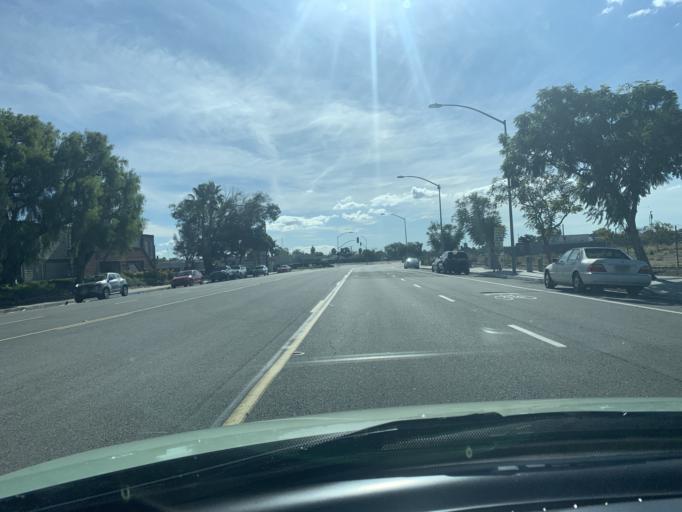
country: US
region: California
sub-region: San Diego County
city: San Diego
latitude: 32.8033
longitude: -117.1288
